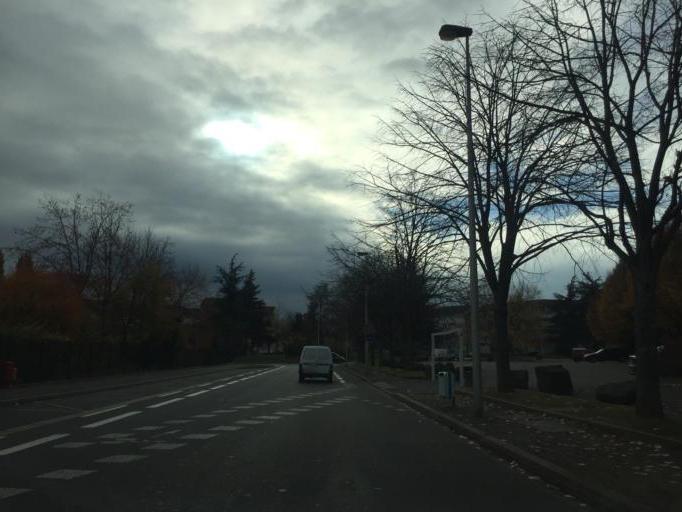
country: FR
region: Rhone-Alpes
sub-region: Departement du Rhone
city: Villefranche-sur-Saone
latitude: 45.9982
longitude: 4.7289
